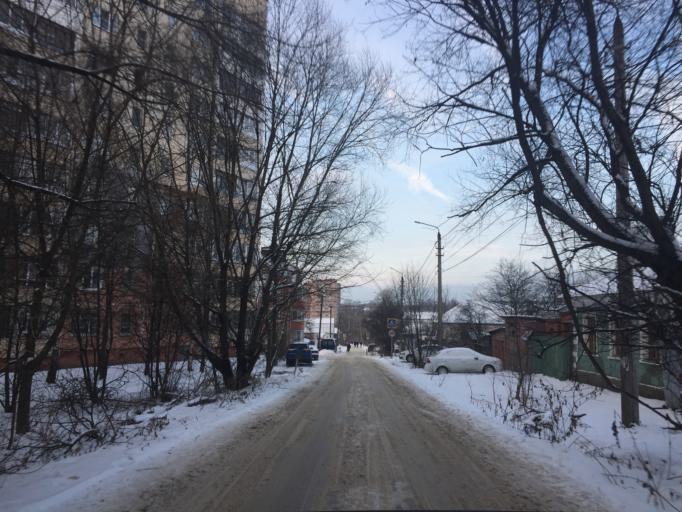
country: RU
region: Tula
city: Tula
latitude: 54.1988
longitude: 37.6779
